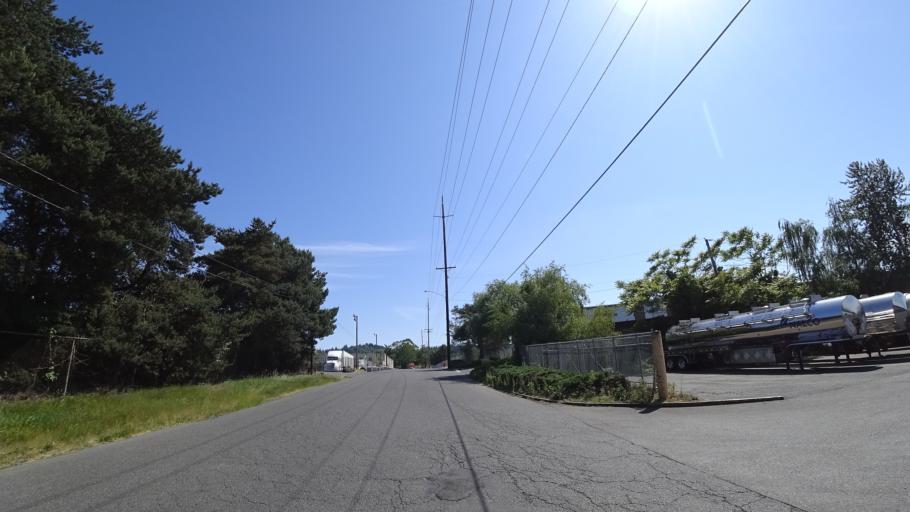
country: US
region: Oregon
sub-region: Multnomah County
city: Lents
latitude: 45.5652
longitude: -122.5684
